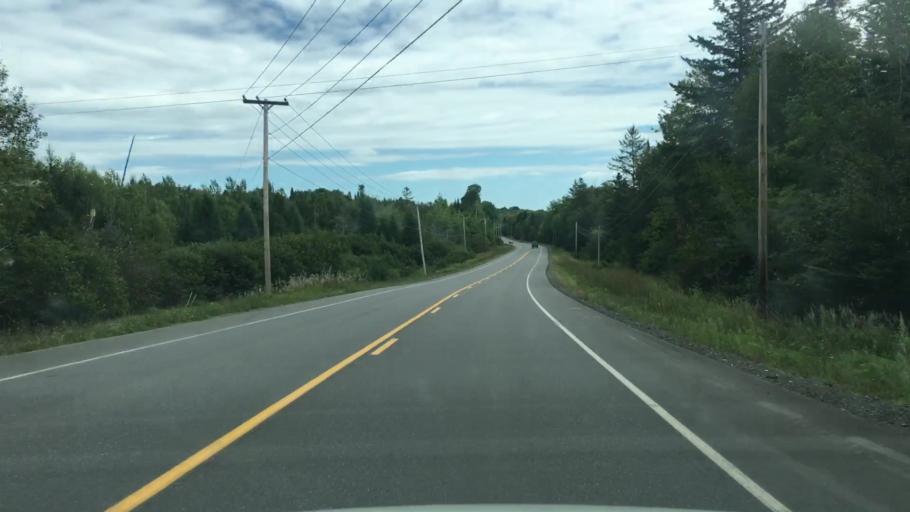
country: US
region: Maine
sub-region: Piscataquis County
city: Milo
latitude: 45.2417
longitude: -69.0357
